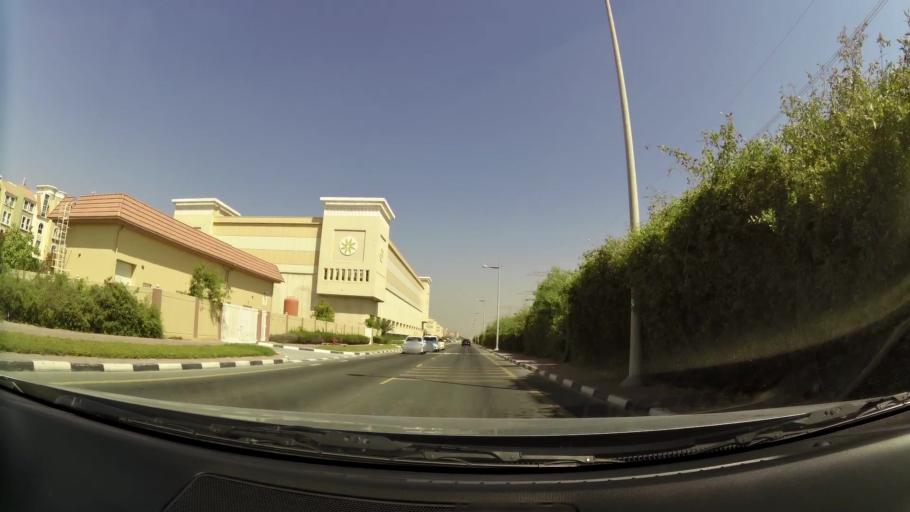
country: AE
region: Dubai
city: Dubai
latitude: 25.0350
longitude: 55.1540
